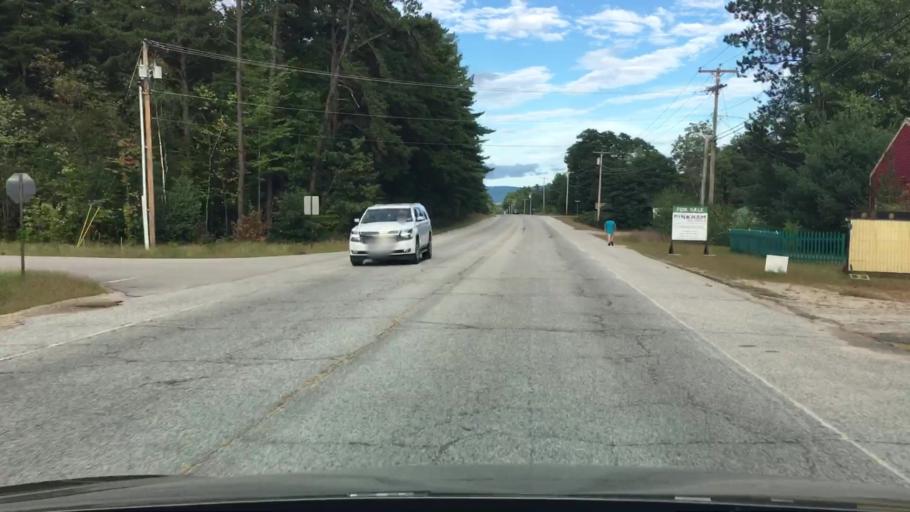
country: US
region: Maine
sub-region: Oxford County
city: Fryeburg
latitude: 44.0202
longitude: -70.9635
